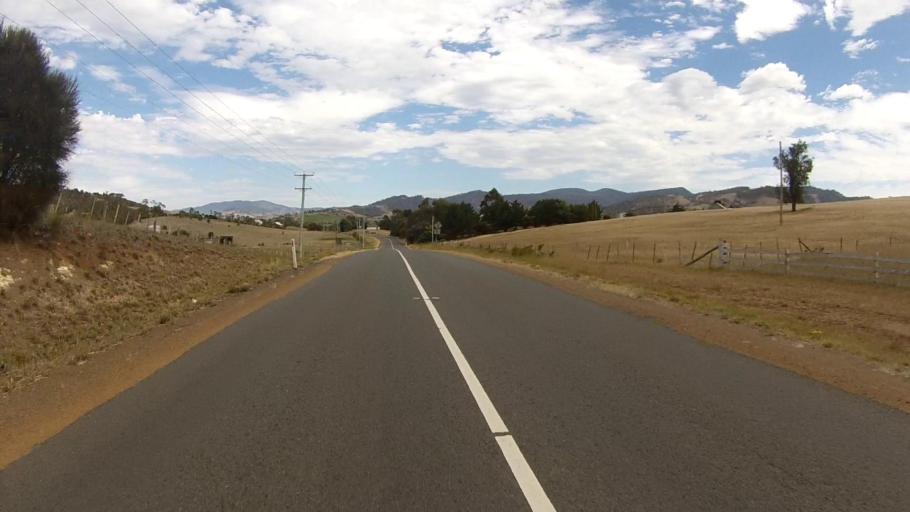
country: AU
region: Tasmania
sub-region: Brighton
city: Old Beach
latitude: -42.6979
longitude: 147.3549
